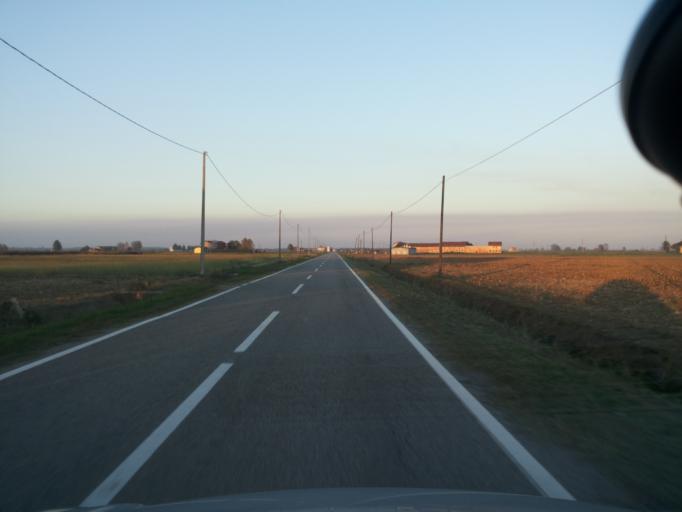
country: IT
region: Piedmont
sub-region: Provincia di Vercelli
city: Santhia
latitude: 45.3748
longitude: 8.1942
